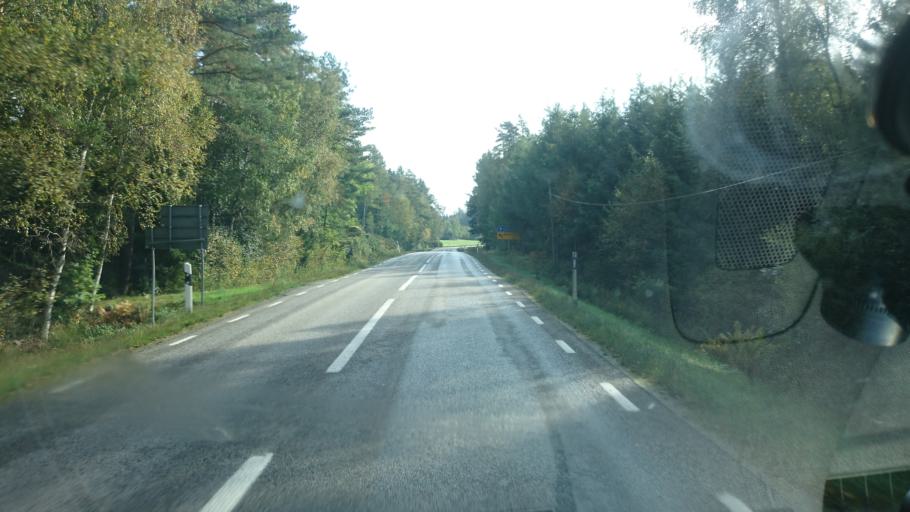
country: SE
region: Vaestra Goetaland
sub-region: Alingsas Kommun
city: Sollebrunn
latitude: 58.1306
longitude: 12.4913
